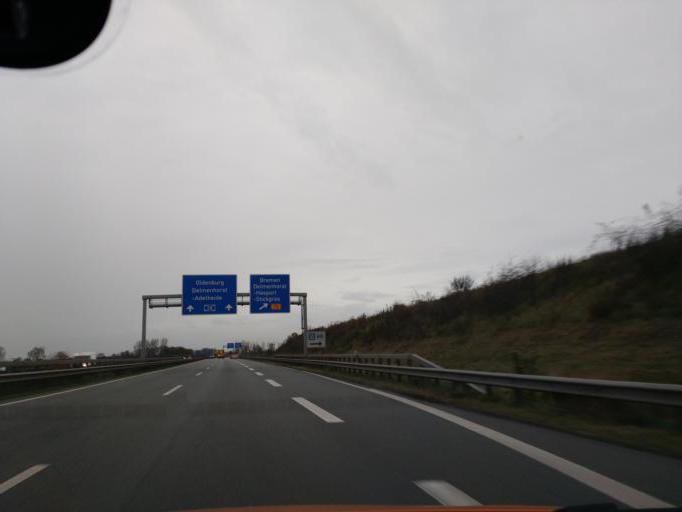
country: DE
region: Lower Saxony
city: Delmenhorst
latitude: 53.0273
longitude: 8.6797
